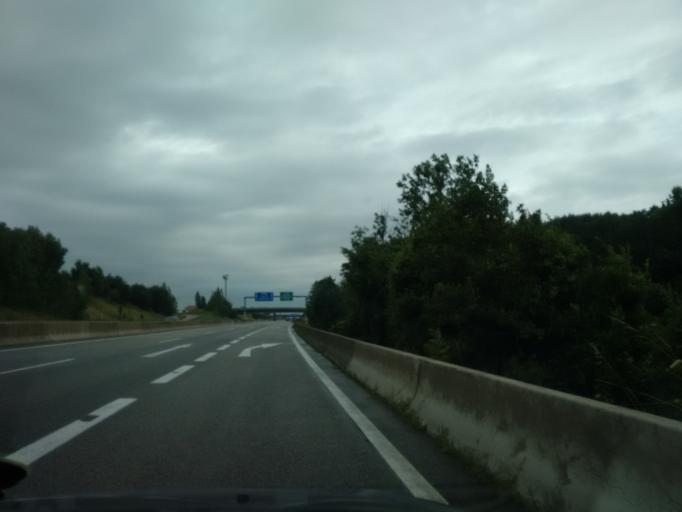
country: AT
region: Upper Austria
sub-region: Wels-Land
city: Sattledt
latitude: 48.0697
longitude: 14.0278
